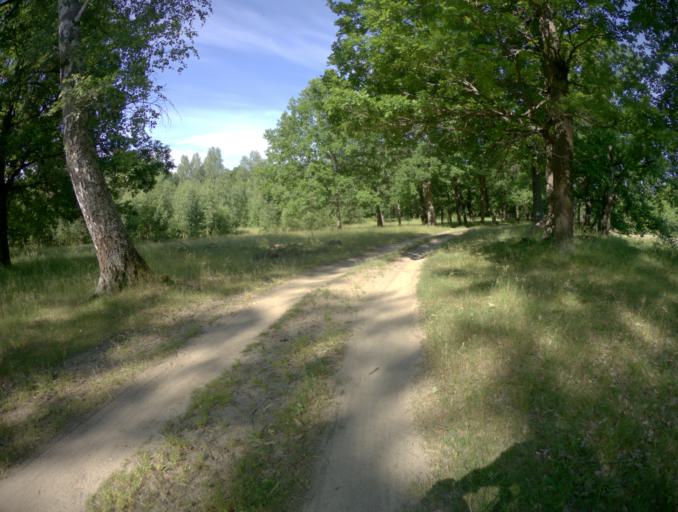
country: RU
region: Ivanovo
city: Talitsy
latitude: 56.5267
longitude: 42.3622
